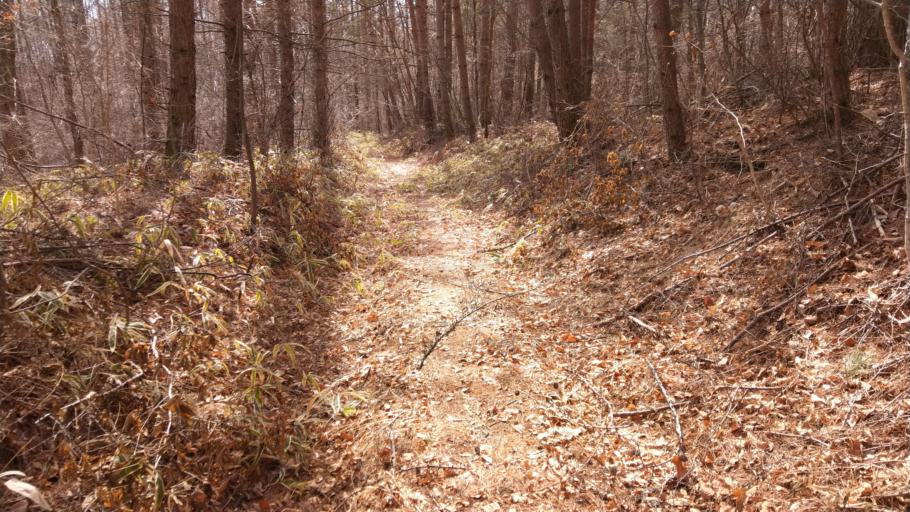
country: JP
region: Nagano
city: Komoro
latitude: 36.3717
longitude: 138.4382
